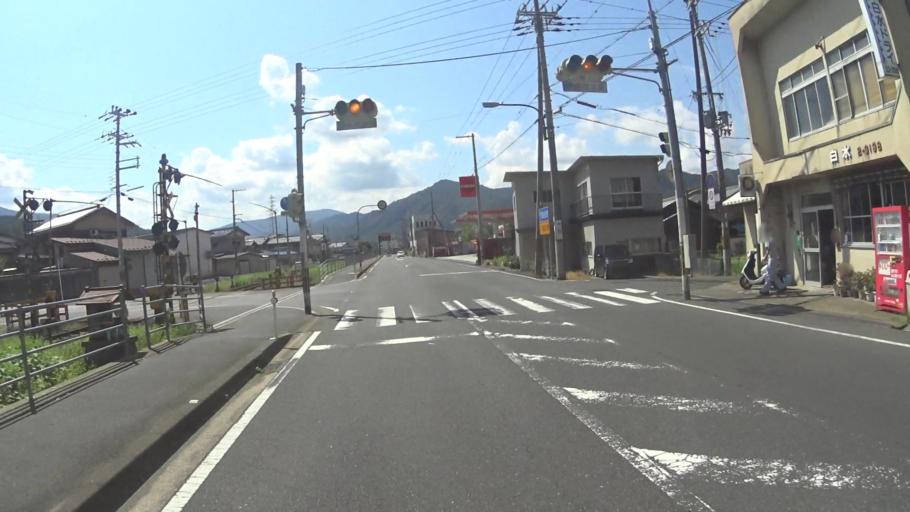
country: JP
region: Kyoto
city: Miyazu
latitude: 35.5384
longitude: 135.2057
